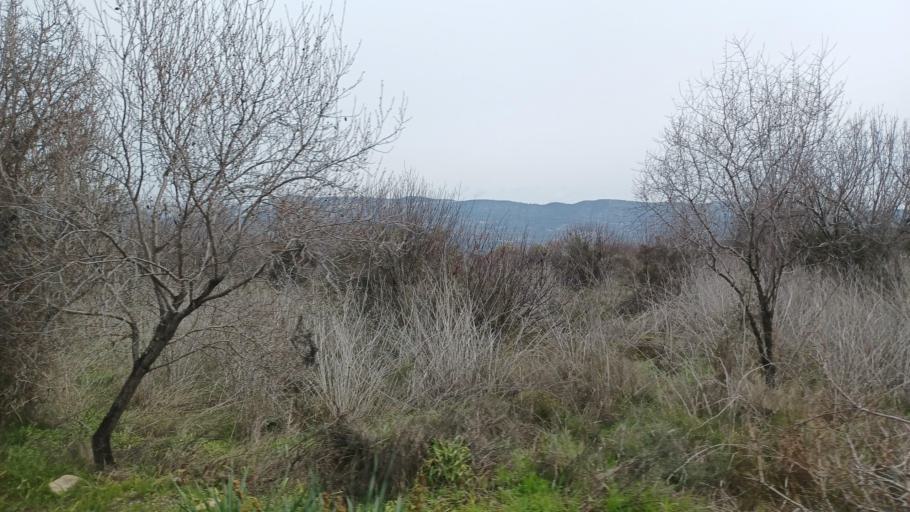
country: CY
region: Limassol
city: Pachna
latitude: 34.8599
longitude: 32.7113
